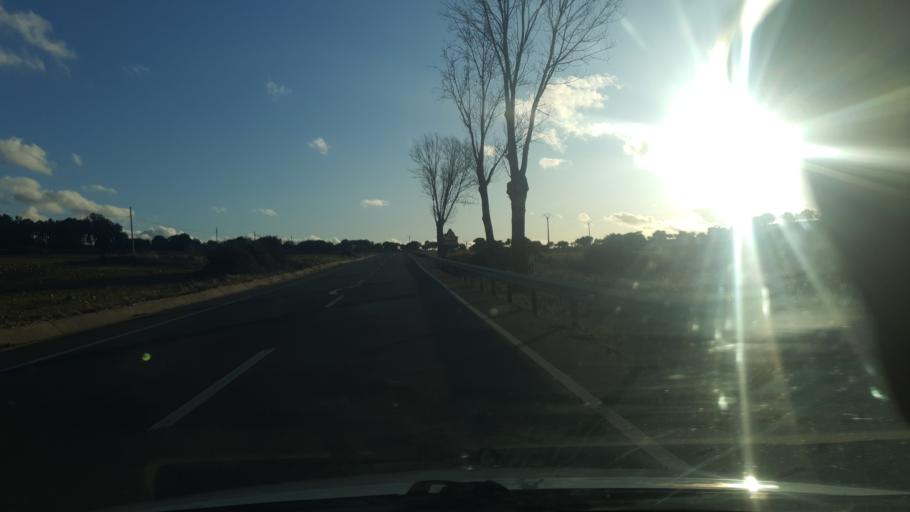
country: ES
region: Castille and Leon
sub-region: Provincia de Avila
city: Mingorria
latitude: 40.7408
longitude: -4.6728
